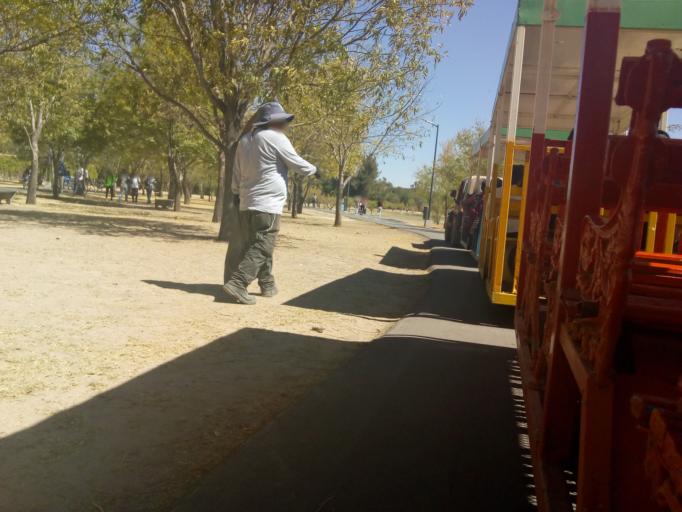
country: MX
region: Guanajuato
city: Leon
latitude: 21.1859
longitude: -101.6791
